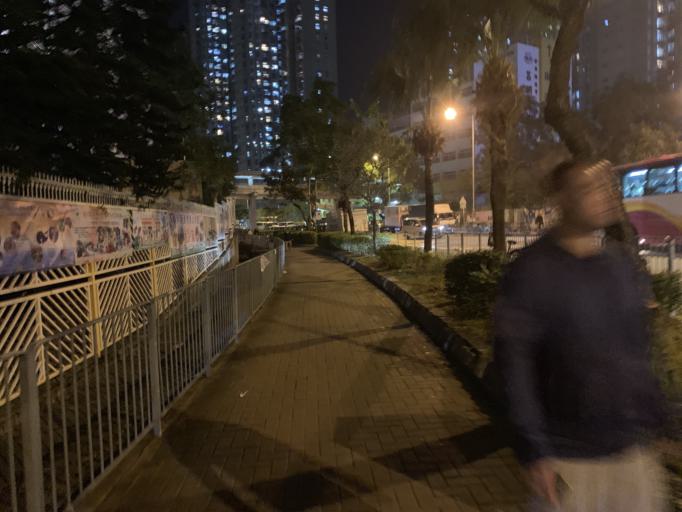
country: HK
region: Tsuen Wan
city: Tsuen Wan
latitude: 22.3617
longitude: 114.1022
